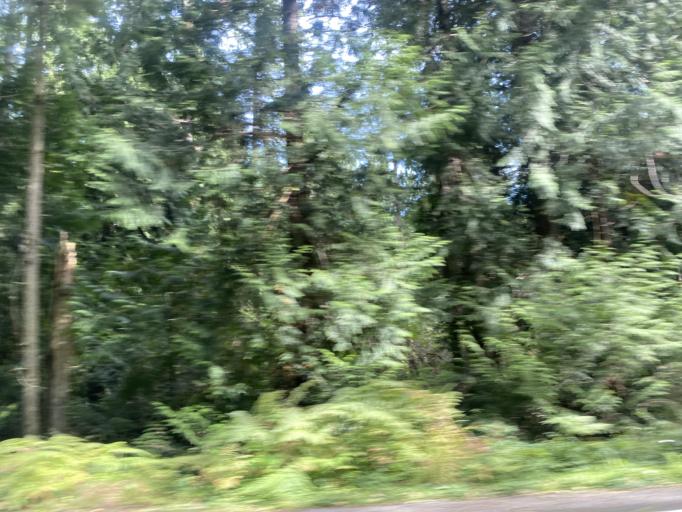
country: US
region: Washington
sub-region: Island County
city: Langley
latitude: 48.0293
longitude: -122.4229
